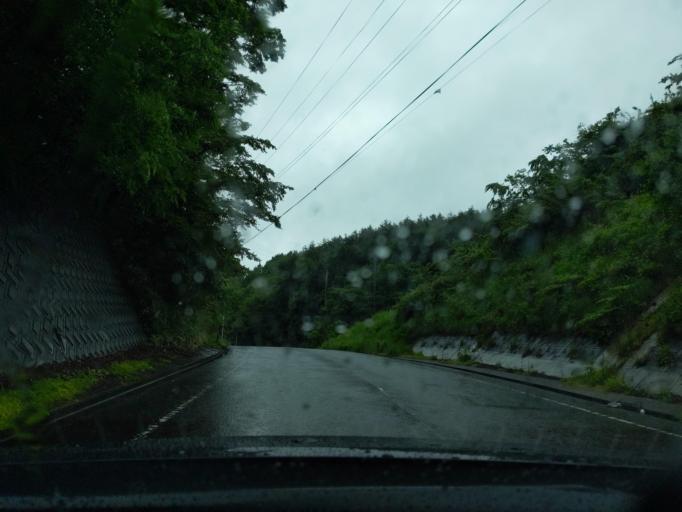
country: JP
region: Fukushima
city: Funehikimachi-funehiki
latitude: 37.5973
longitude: 140.6018
